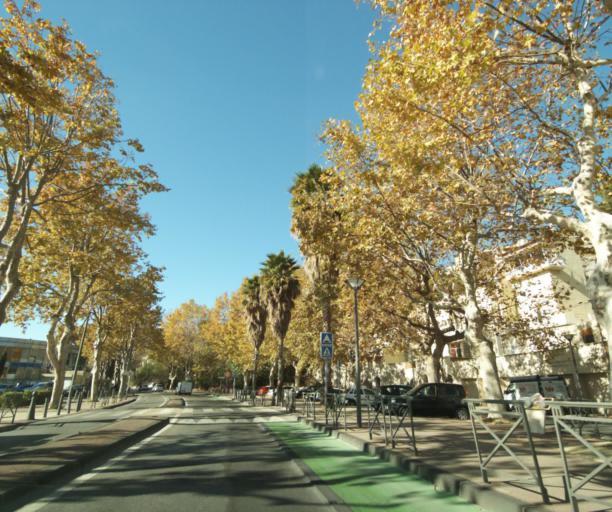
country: FR
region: Provence-Alpes-Cote d'Azur
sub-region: Departement des Bouches-du-Rhone
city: Marseille 16
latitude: 43.3621
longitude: 5.3100
